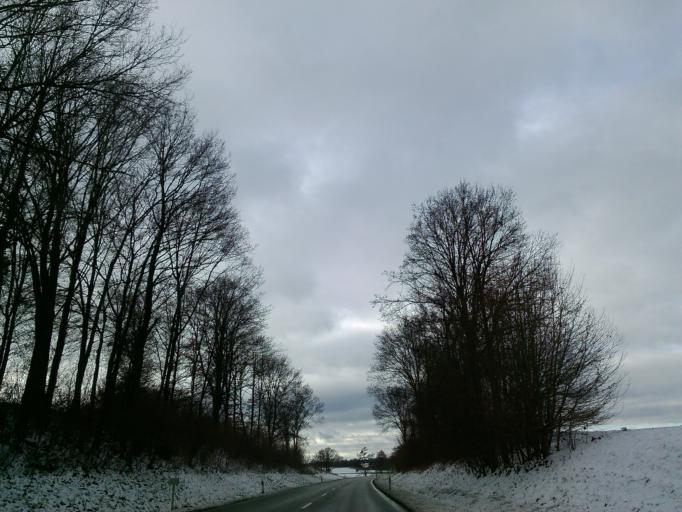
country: DE
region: Bavaria
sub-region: Swabia
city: Zusmarshausen
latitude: 48.3911
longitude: 10.5915
